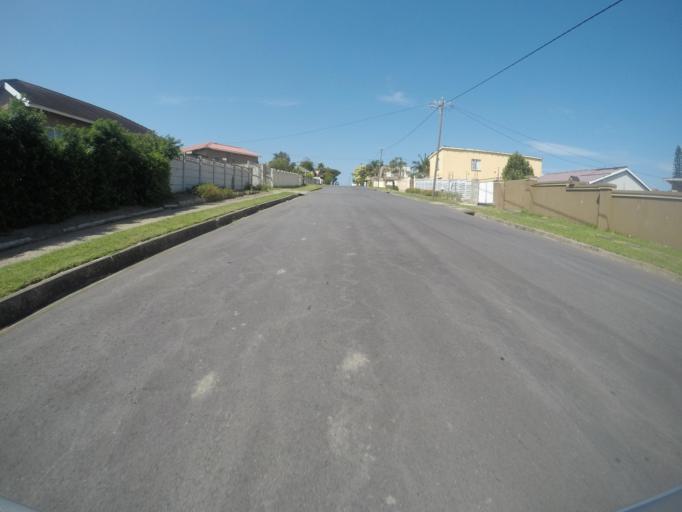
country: ZA
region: Eastern Cape
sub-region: Buffalo City Metropolitan Municipality
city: East London
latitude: -32.9804
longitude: 27.8725
